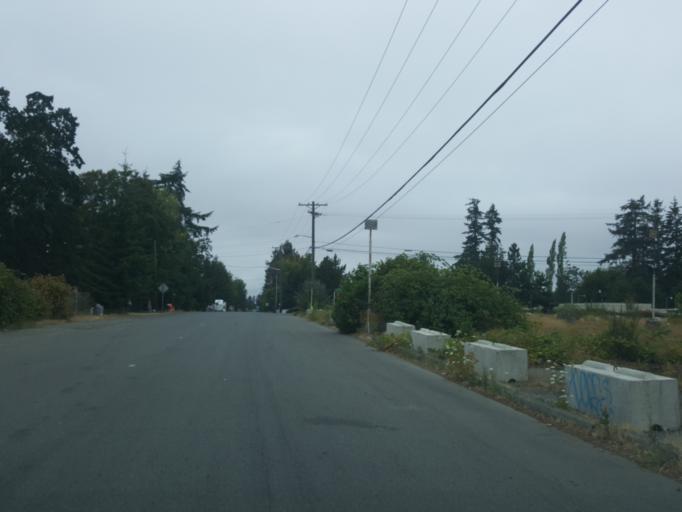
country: US
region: Washington
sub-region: Pierce County
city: Parkland
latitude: 47.1642
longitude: -122.4684
